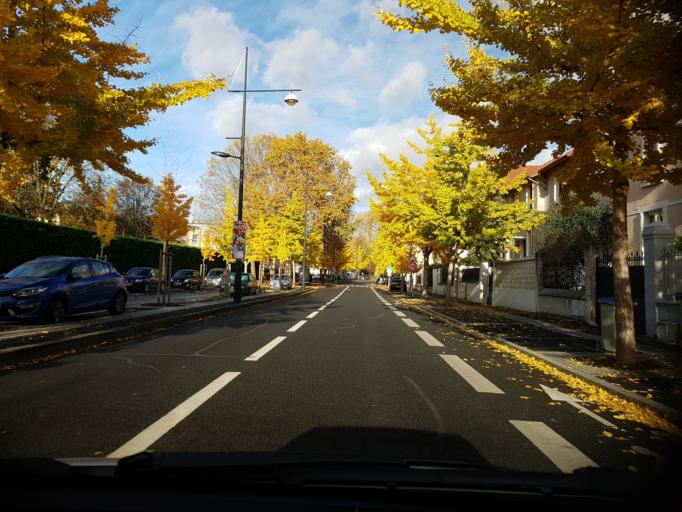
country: FR
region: Ile-de-France
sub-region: Departement du Val-de-Marne
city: Cachan
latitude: 48.7972
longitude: 2.3338
